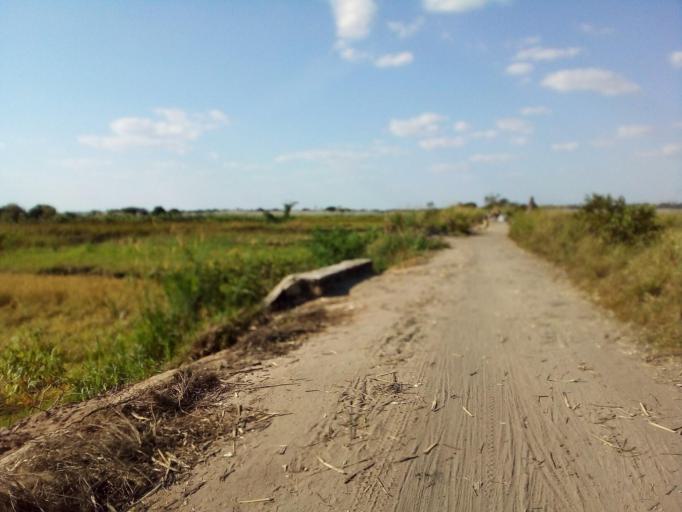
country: MZ
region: Zambezia
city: Quelimane
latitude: -17.5851
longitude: 36.8418
